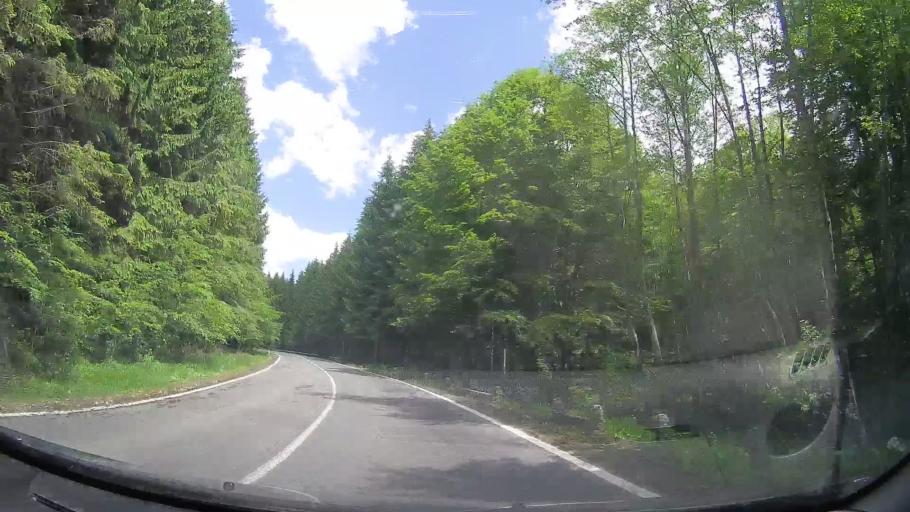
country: RO
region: Brasov
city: Crivina
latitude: 45.4593
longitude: 25.9535
